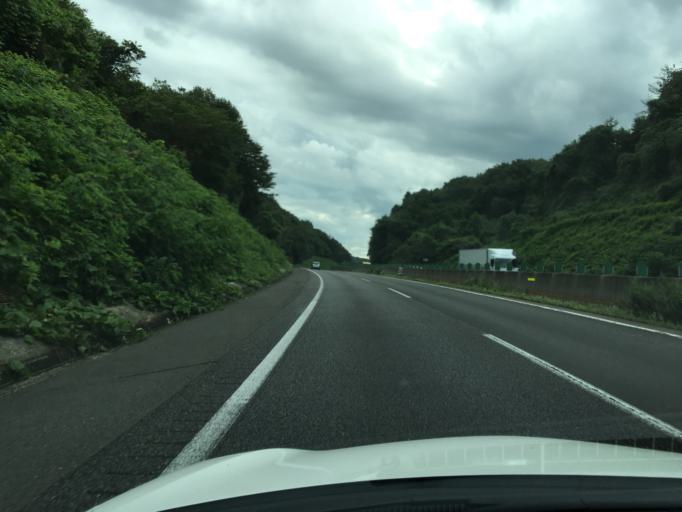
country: JP
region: Fukushima
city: Nihommatsu
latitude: 37.6282
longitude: 140.4320
